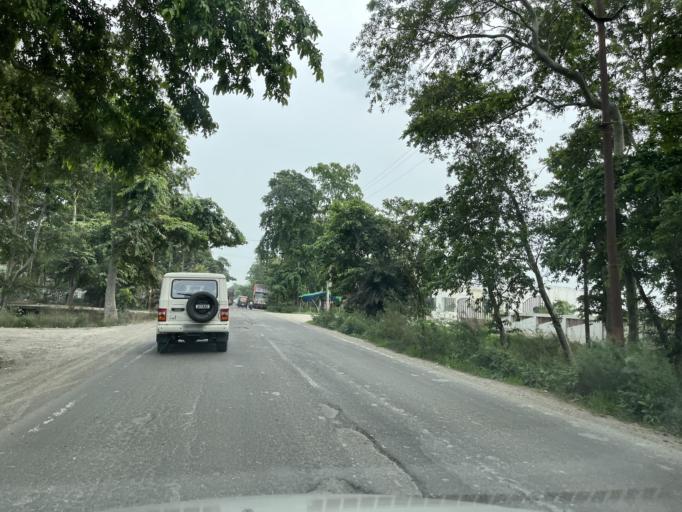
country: IN
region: Uttar Pradesh
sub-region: Rampur
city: Bilaspur
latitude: 29.0275
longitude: 79.2675
